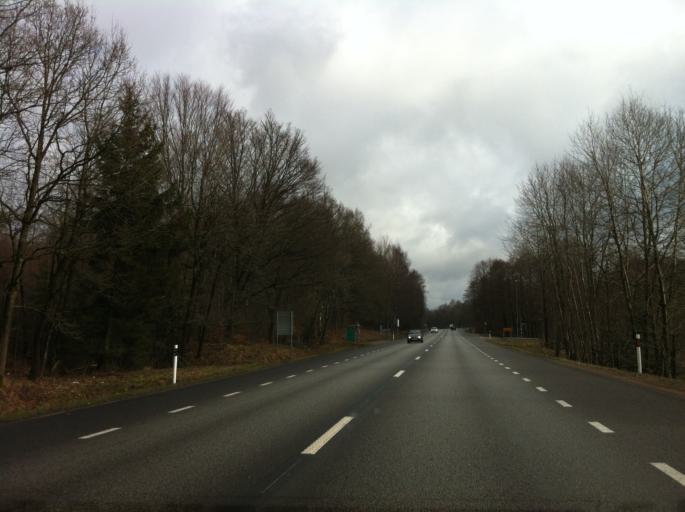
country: SE
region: Halland
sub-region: Halmstads Kommun
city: Aled
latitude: 56.7489
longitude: 12.9367
